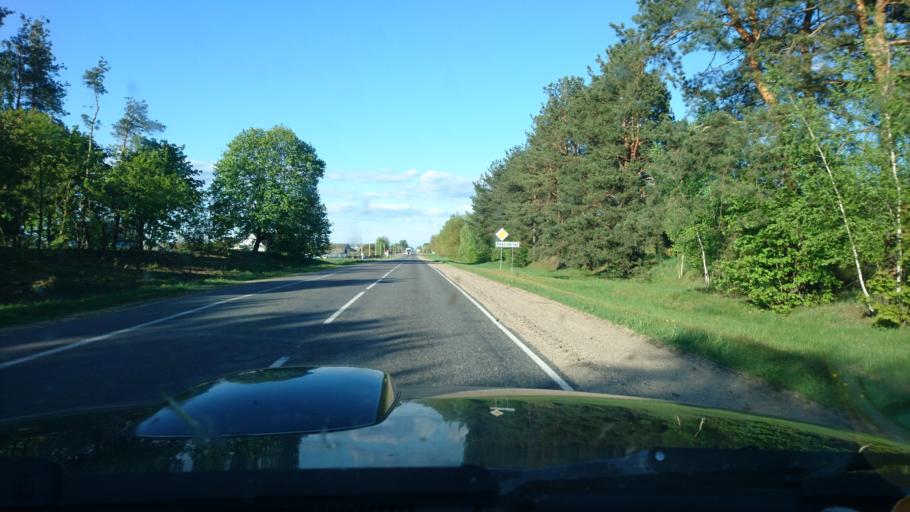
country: BY
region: Brest
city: Ivatsevichy
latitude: 52.6928
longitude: 25.3045
